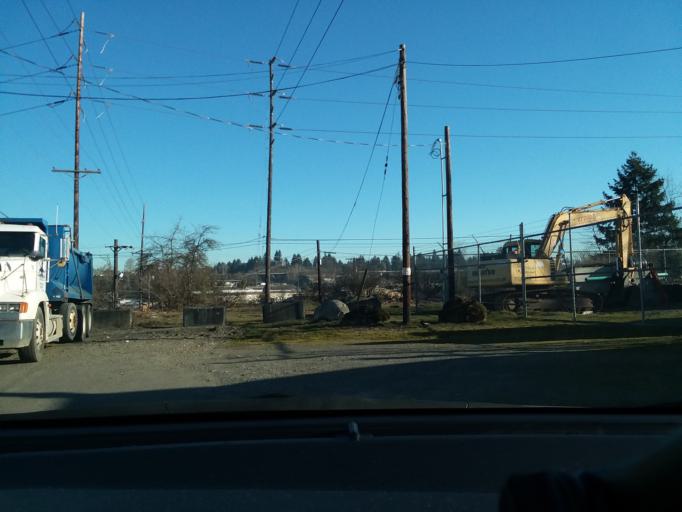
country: US
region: Washington
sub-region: Pierce County
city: Tacoma
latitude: 47.2278
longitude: -122.4763
